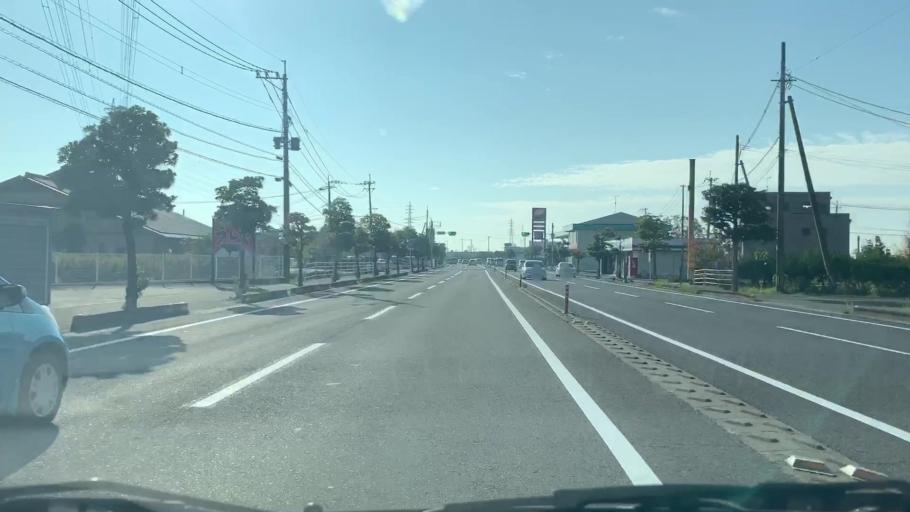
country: JP
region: Saga Prefecture
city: Saga-shi
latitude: 33.3002
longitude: 130.2804
